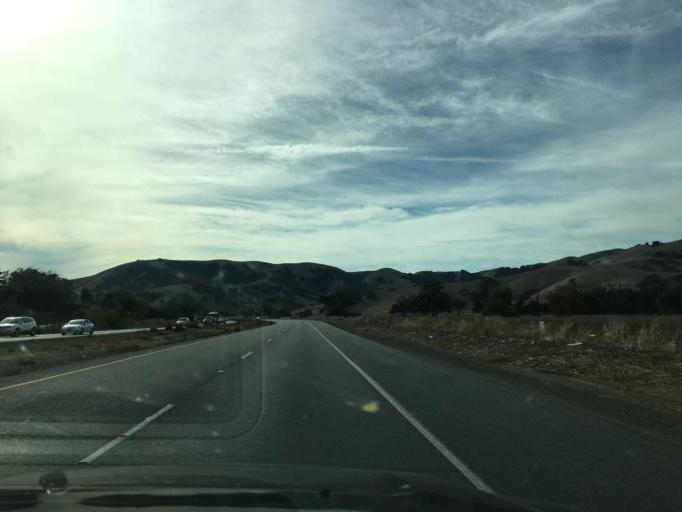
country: US
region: California
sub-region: San Benito County
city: Hollister
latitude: 36.9983
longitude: -121.3759
